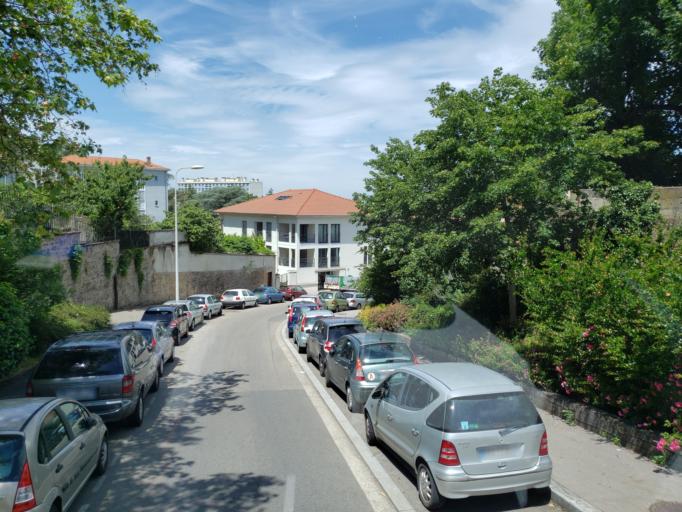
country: FR
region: Rhone-Alpes
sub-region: Departement du Rhone
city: Sainte-Foy-les-Lyon
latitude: 45.7550
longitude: 4.8120
